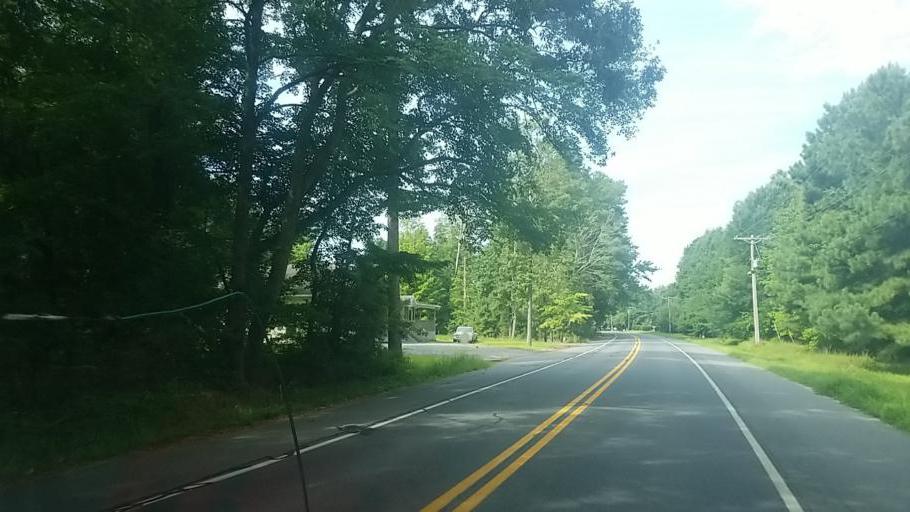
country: US
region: Delaware
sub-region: Sussex County
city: Long Neck
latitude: 38.5439
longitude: -75.1752
